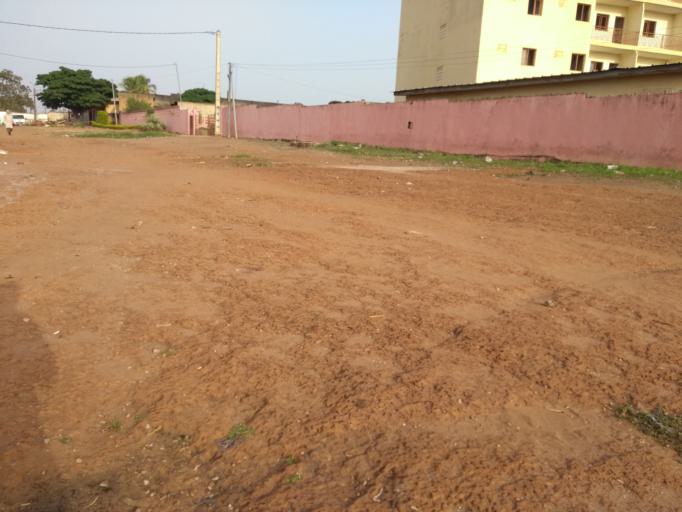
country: CI
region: Vallee du Bandama
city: Bouake
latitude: 7.7075
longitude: -5.0279
